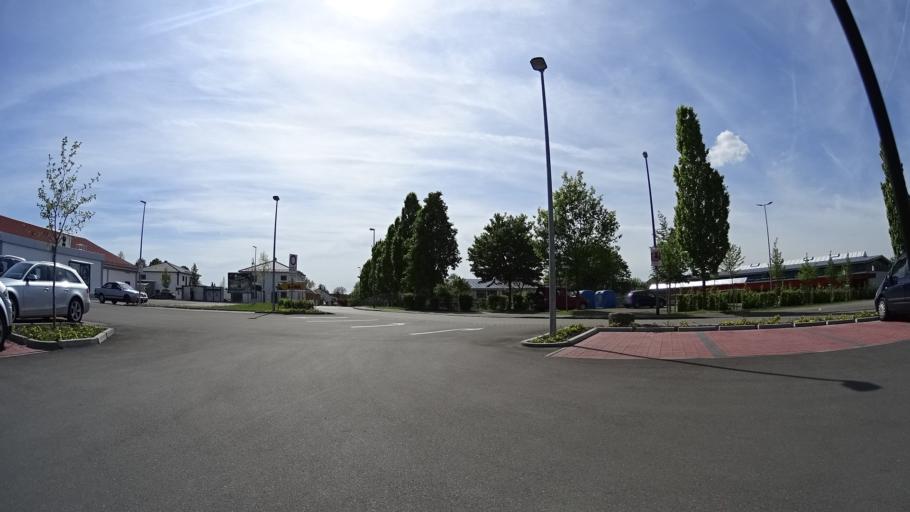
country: DE
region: Bavaria
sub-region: Swabia
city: Pfaffenhofen an der Roth
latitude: 48.3485
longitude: 10.1618
